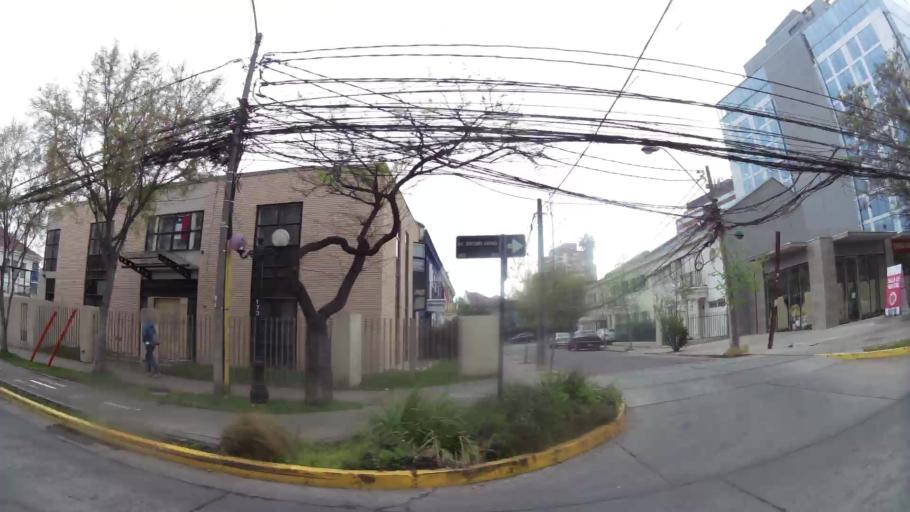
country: CL
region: Santiago Metropolitan
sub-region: Provincia de Santiago
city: Santiago
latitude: -33.4310
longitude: -70.6165
